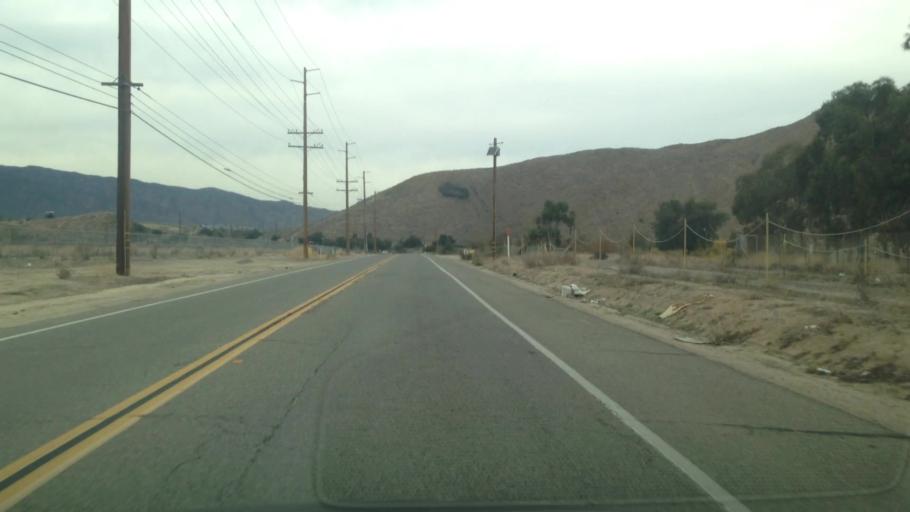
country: US
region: California
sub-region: Riverside County
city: El Cerrito
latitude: 33.7465
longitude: -117.4440
